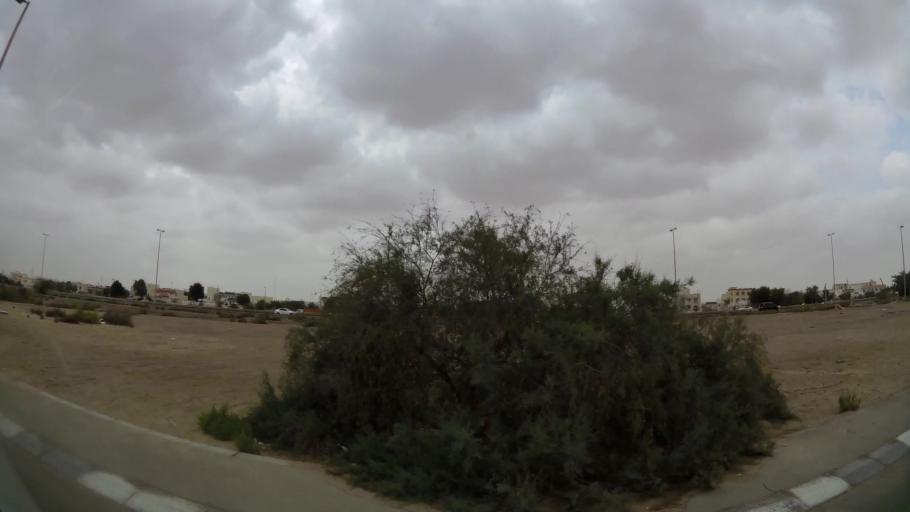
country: AE
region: Abu Dhabi
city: Abu Dhabi
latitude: 24.3288
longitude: 54.6392
